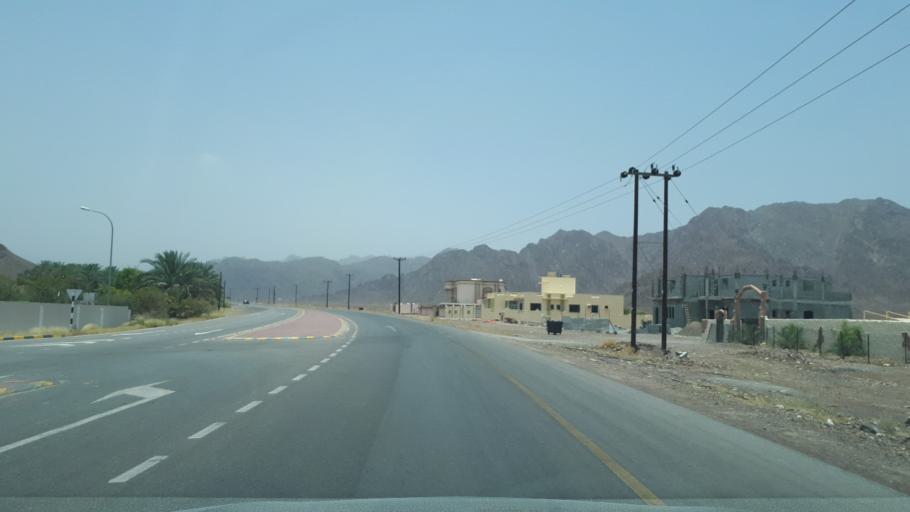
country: OM
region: Al Batinah
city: Rustaq
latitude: 23.4303
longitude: 57.2784
